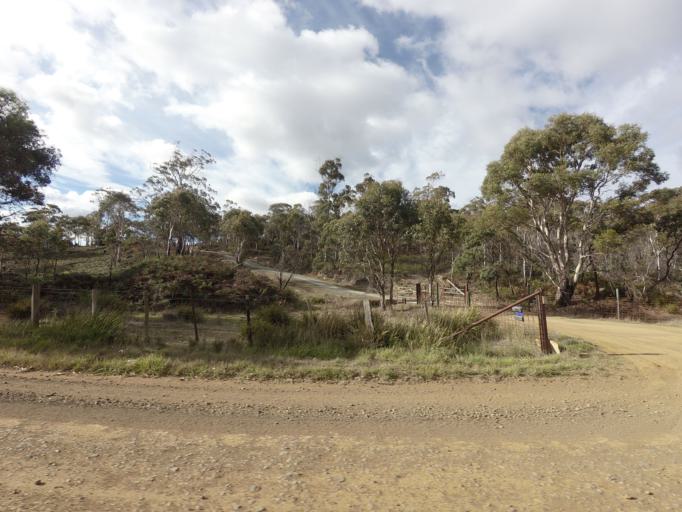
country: AU
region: Tasmania
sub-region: Brighton
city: Bridgewater
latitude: -42.4794
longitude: 147.2944
